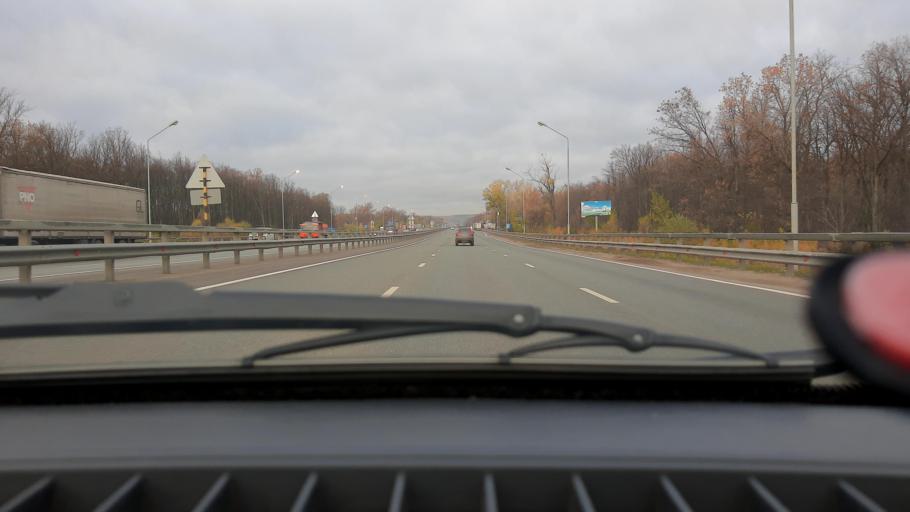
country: RU
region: Bashkortostan
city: Ufa
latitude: 54.6633
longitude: 55.8699
